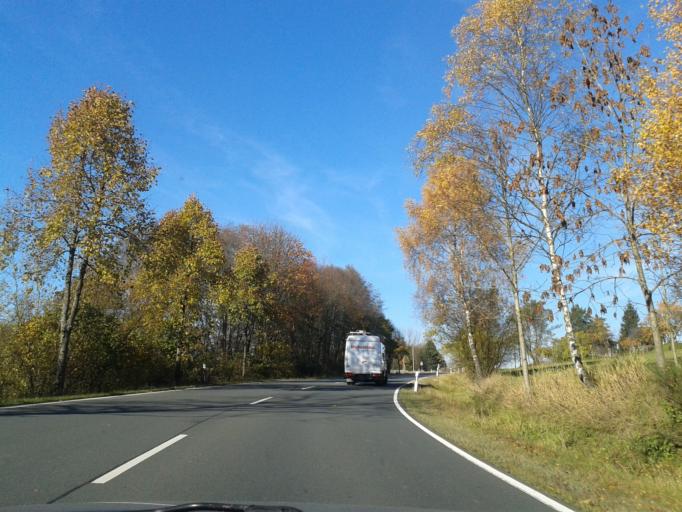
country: DE
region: North Rhine-Westphalia
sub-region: Regierungsbezirk Arnsberg
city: Erndtebruck
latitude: 50.9791
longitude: 8.3281
